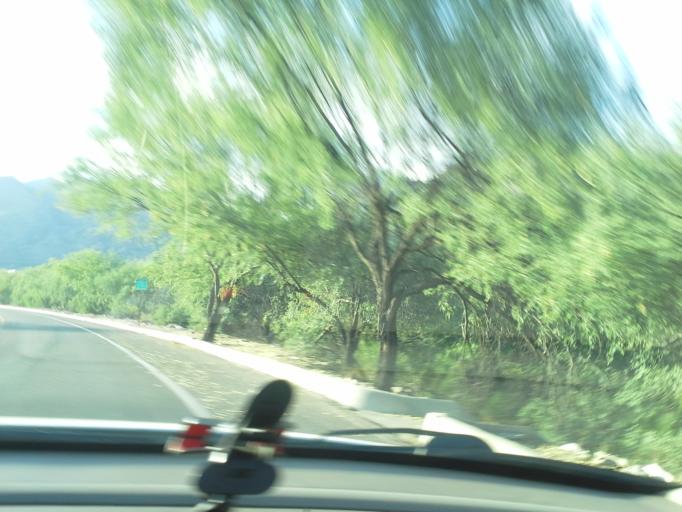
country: US
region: Arizona
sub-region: Pima County
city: Catalina Foothills
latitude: 32.3183
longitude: -110.8494
